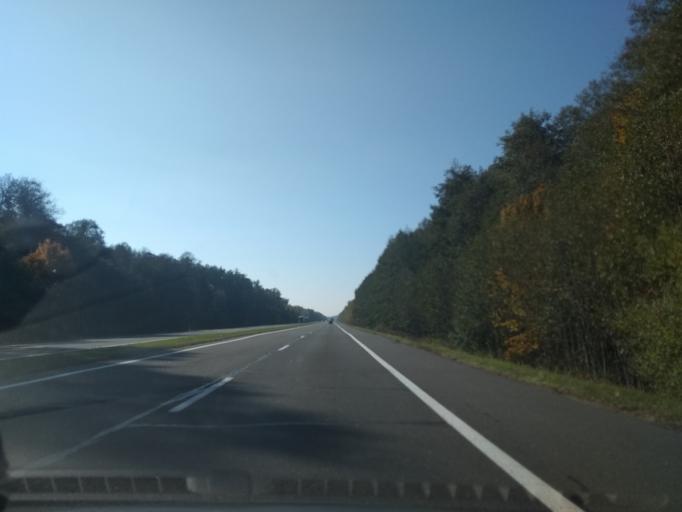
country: BY
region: Brest
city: Ivatsevichy
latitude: 52.8464
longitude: 25.6317
